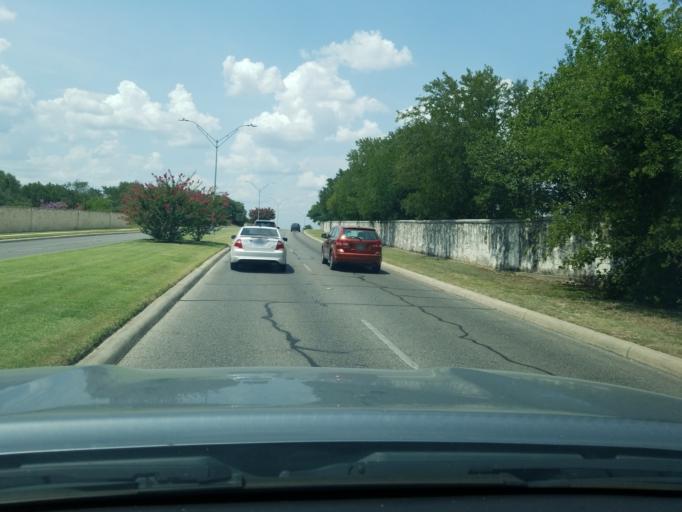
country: US
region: Texas
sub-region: Bexar County
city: Timberwood Park
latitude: 29.6557
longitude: -98.4807
